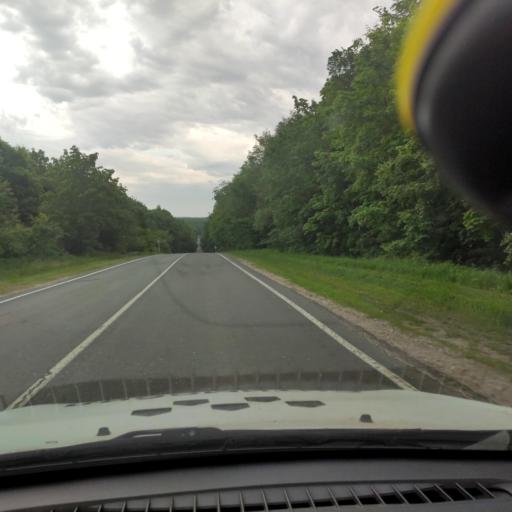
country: RU
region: Samara
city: Zhigulevsk
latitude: 53.3395
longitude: 49.4910
